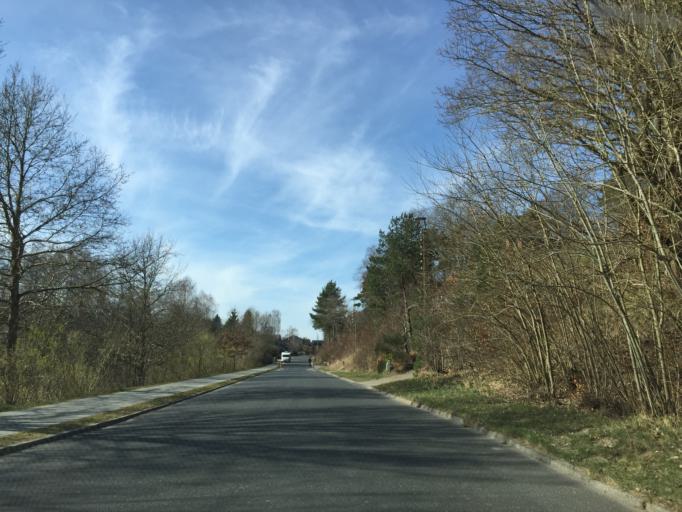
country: DK
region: Central Jutland
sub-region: Silkeborg Kommune
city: Silkeborg
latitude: 56.1908
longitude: 9.5408
